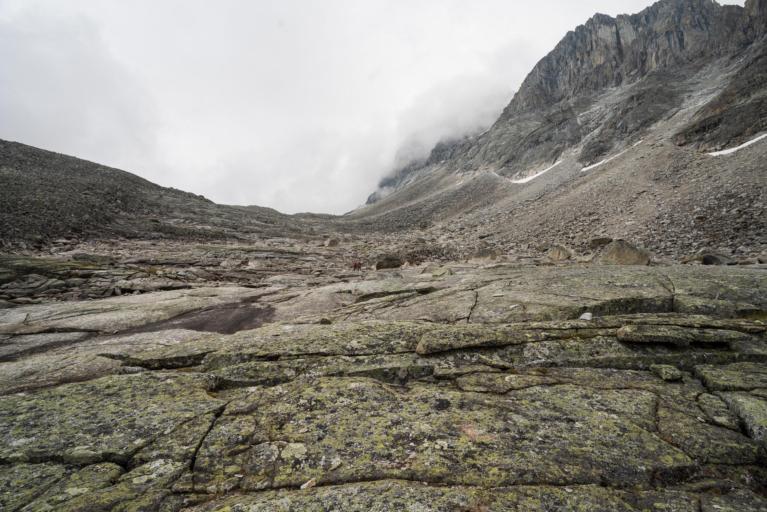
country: RU
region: Transbaikal Territory
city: Chara
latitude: 56.8682
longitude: 117.5910
